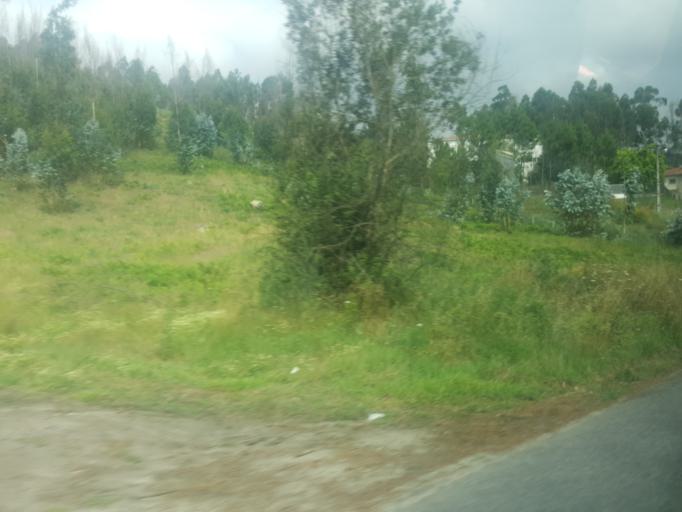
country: PT
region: Porto
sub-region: Marco de Canaveses
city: Marco de Canavezes
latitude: 41.1744
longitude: -8.1912
